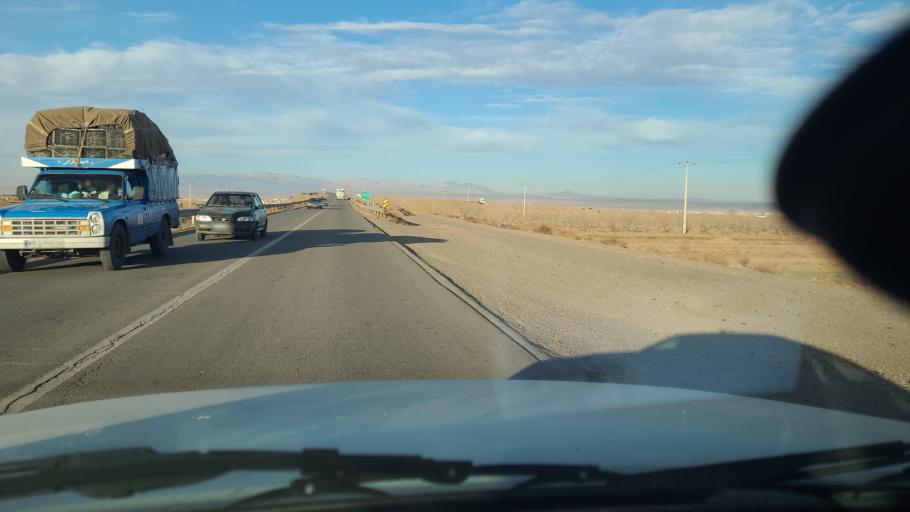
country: IR
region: Razavi Khorasan
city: Neqab
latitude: 36.5996
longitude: 57.5888
